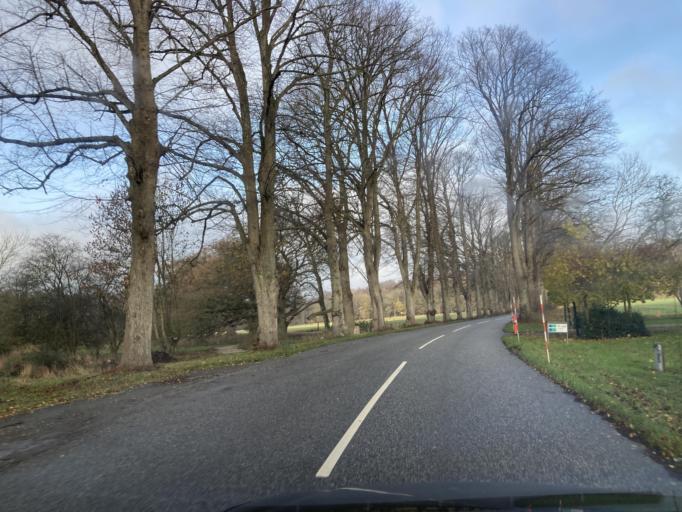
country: DK
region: Zealand
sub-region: Lolland Kommune
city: Rodby
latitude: 54.7611
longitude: 11.3564
